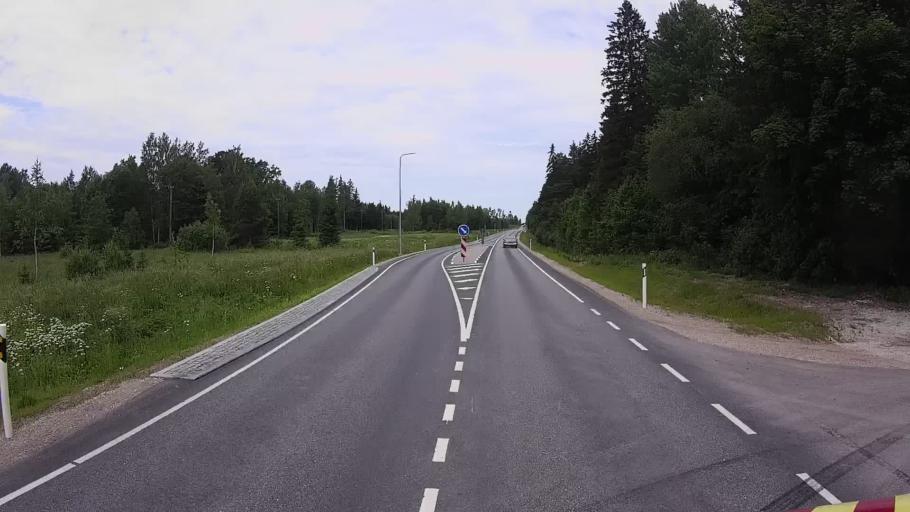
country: EE
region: Viljandimaa
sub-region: Viljandi linn
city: Viljandi
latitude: 58.2475
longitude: 25.5925
